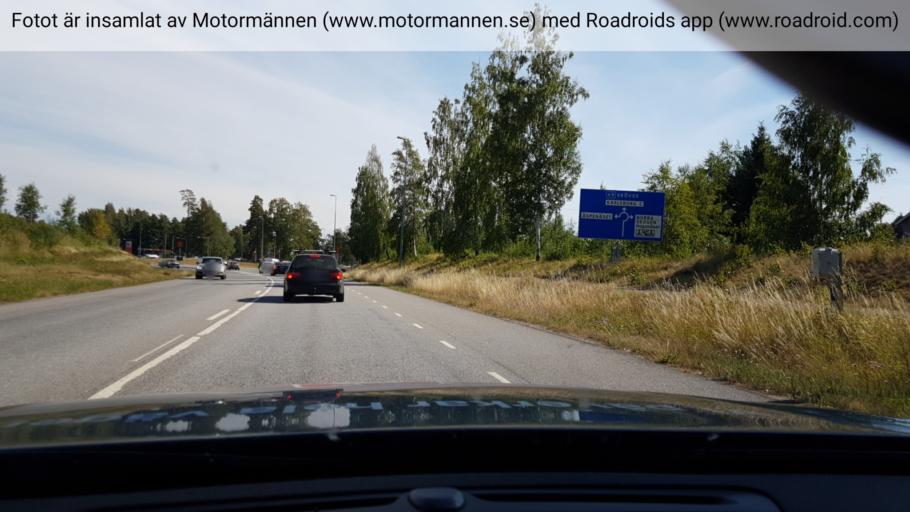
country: SE
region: Vaestra Goetaland
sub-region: Karlsborgs Kommun
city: Karlsborg
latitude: 58.5473
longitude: 14.4996
